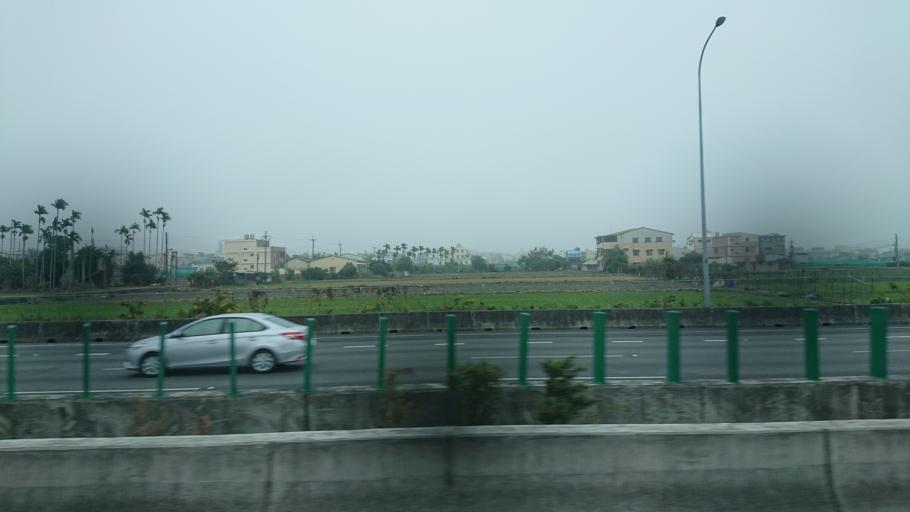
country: TW
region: Taiwan
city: Fengyuan
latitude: 24.3072
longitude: 120.6993
